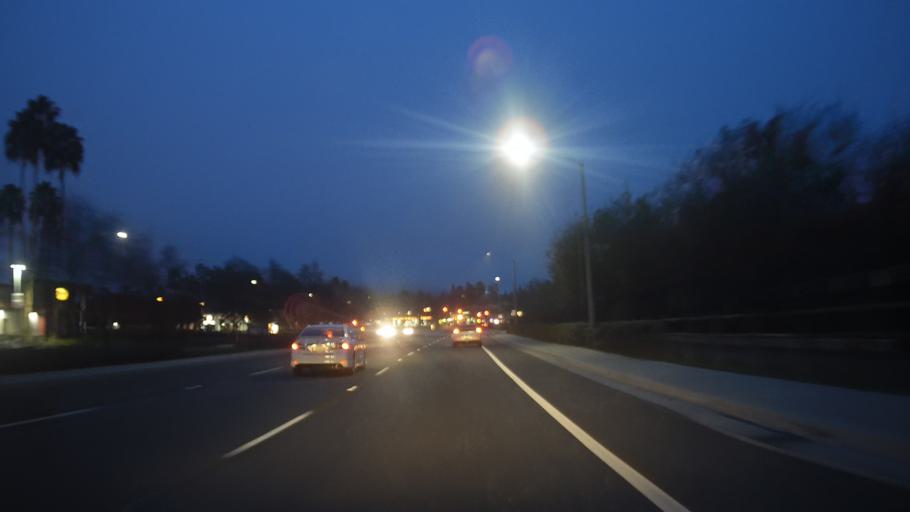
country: US
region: California
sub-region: San Diego County
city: Rancho San Diego
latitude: 32.7437
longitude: -116.9322
